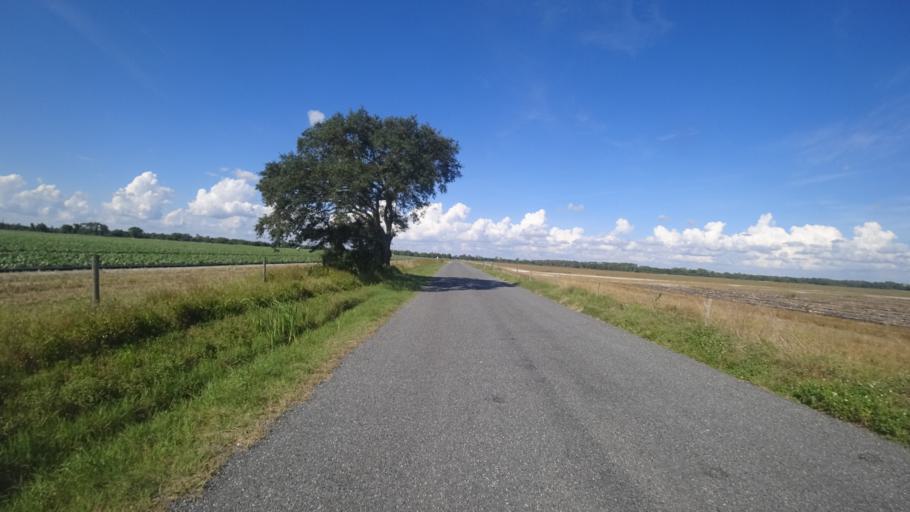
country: US
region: Florida
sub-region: Sarasota County
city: The Meadows
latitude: 27.4332
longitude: -82.2871
